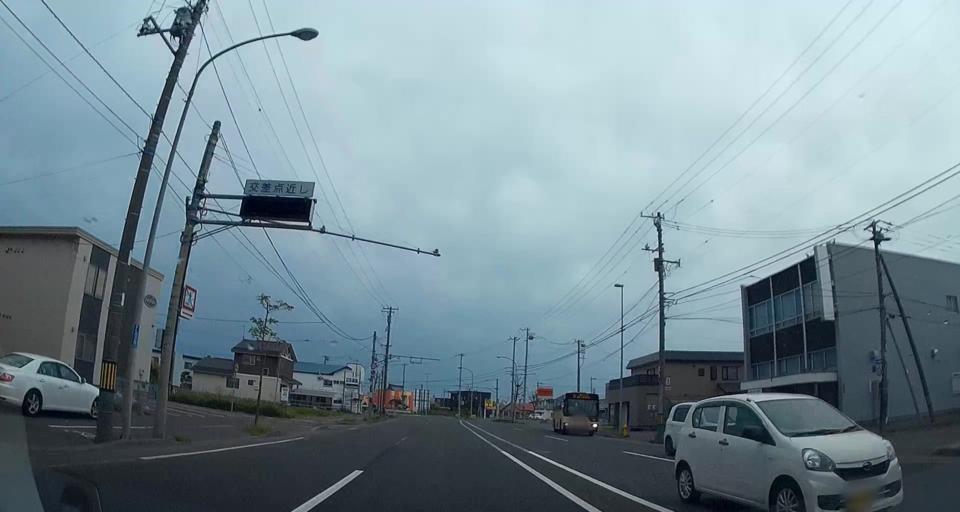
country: JP
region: Hokkaido
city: Tomakomai
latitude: 42.6285
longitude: 141.5939
